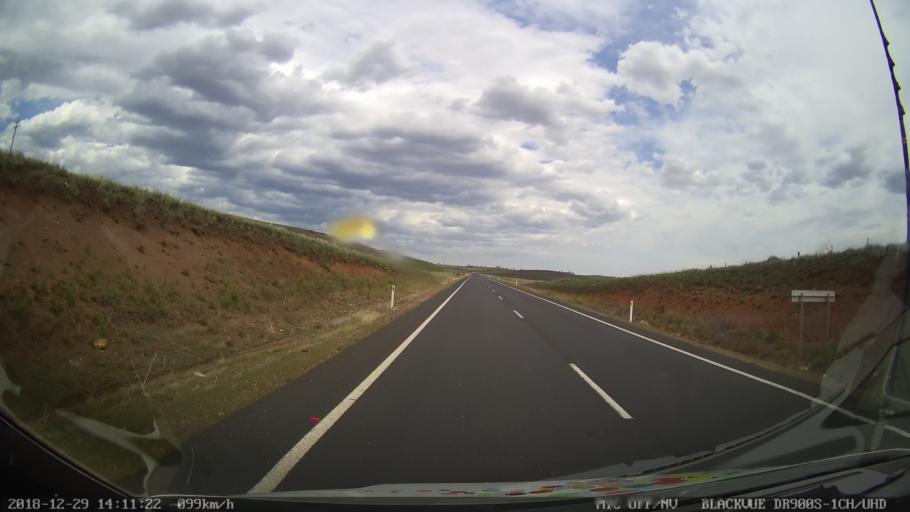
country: AU
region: New South Wales
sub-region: Cooma-Monaro
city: Cooma
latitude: -36.4049
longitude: 149.2200
